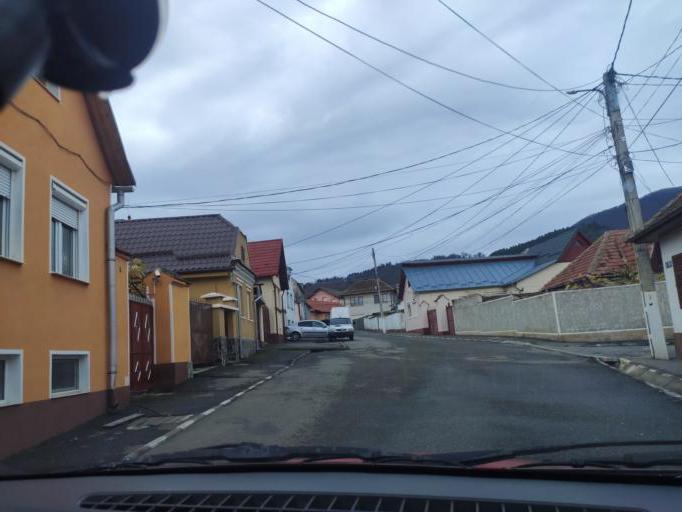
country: RO
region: Brasov
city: Codlea
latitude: 45.6962
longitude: 25.4404
